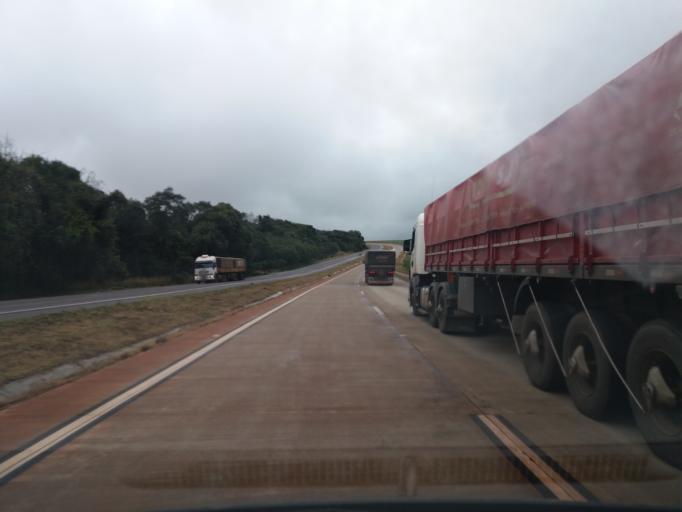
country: BR
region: Parana
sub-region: Cascavel
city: Cascavel
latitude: -25.0655
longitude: -53.5682
